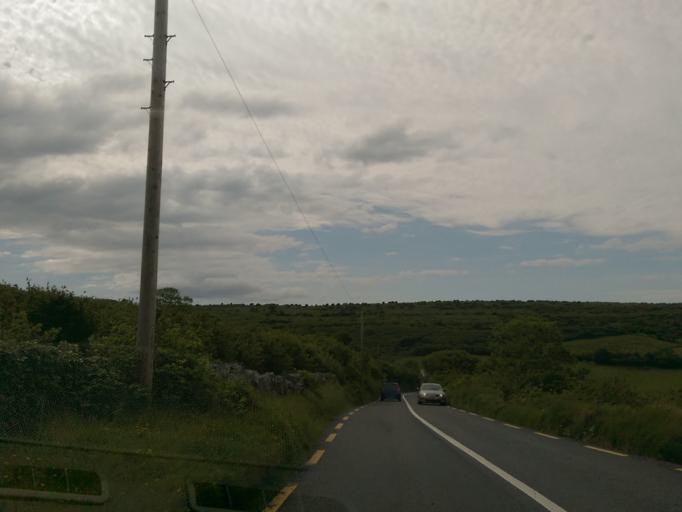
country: IE
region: Connaught
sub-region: County Galway
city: Bearna
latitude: 53.0698
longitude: -9.1843
